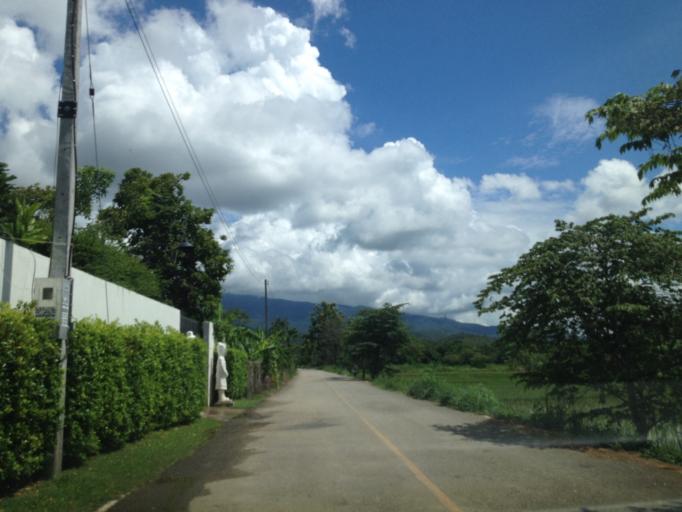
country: TH
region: Chiang Mai
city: Hang Dong
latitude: 18.7189
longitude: 98.9078
